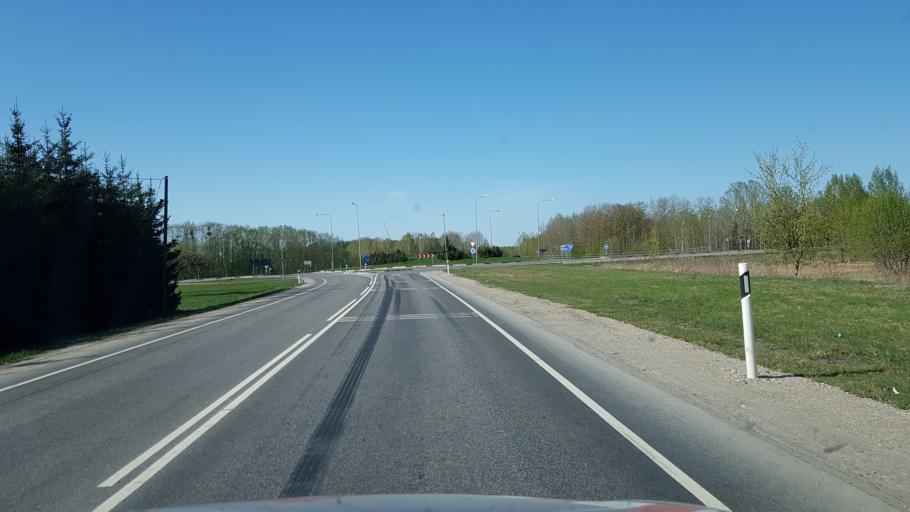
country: EE
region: Viljandimaa
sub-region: Viljandi linn
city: Viljandi
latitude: 58.3544
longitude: 25.5597
